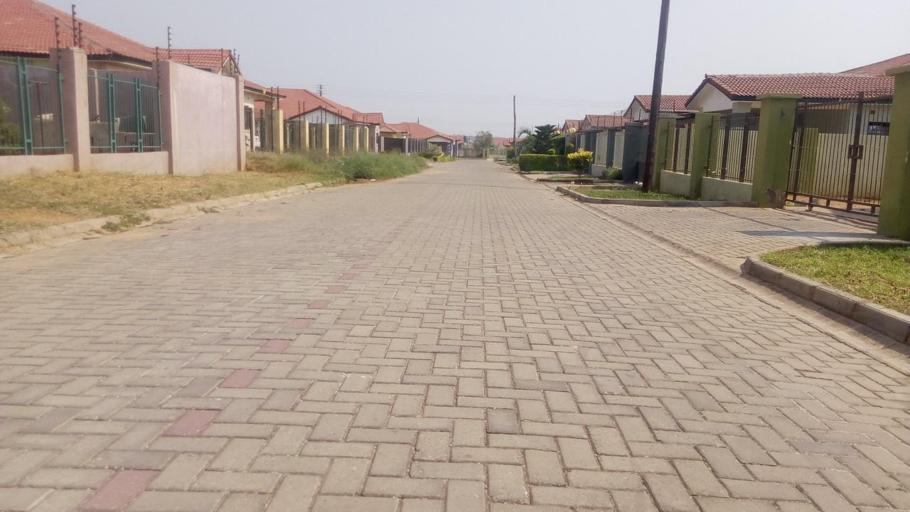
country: ZM
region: Lusaka
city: Lusaka
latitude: -15.3609
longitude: 28.2823
